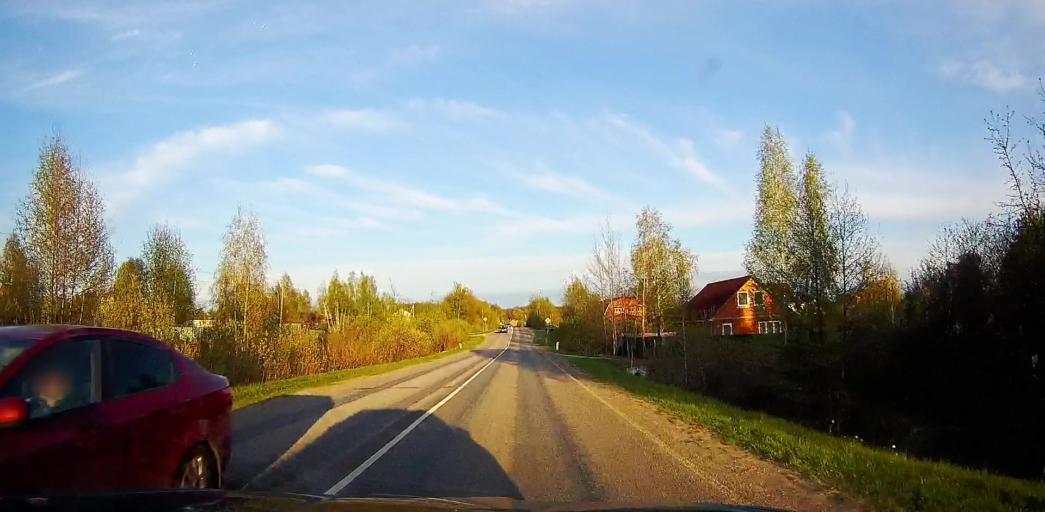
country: RU
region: Moskovskaya
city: Meshcherino
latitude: 55.2468
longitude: 38.3017
